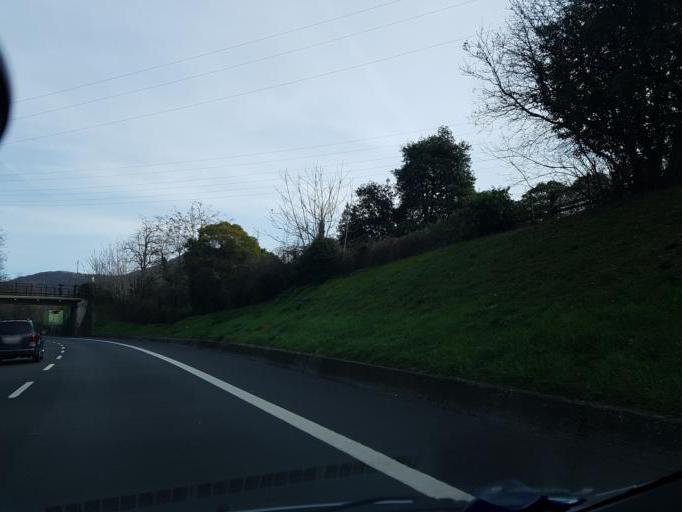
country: IT
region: Liguria
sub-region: Provincia di Genova
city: Manesseno
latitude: 44.4804
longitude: 8.9167
